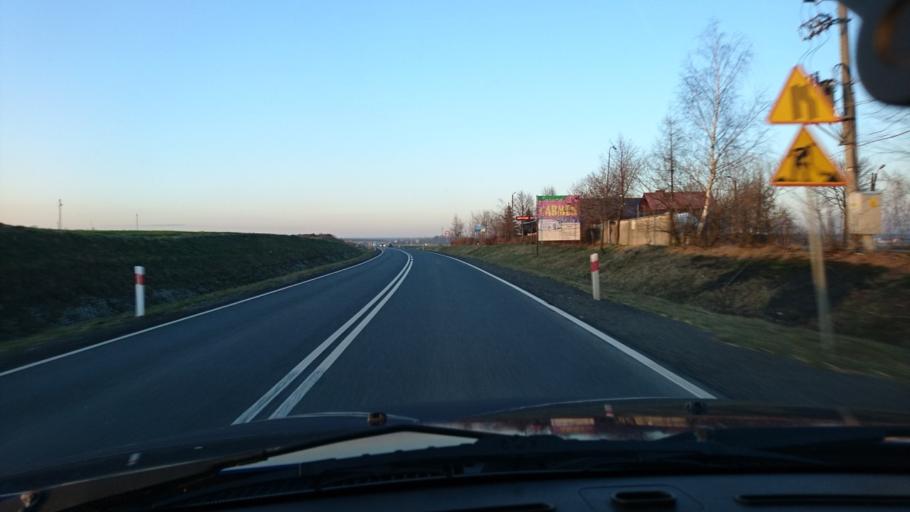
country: PL
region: Silesian Voivodeship
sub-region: Powiat gliwicki
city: Wielowies
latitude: 50.4940
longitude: 18.6075
